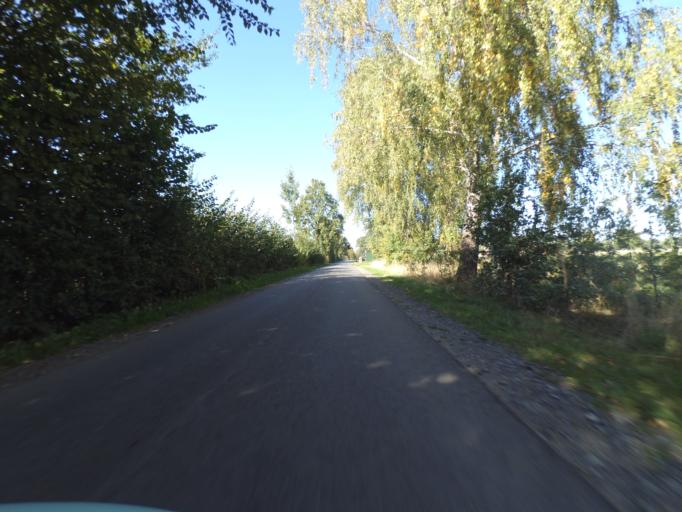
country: DE
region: North Rhine-Westphalia
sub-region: Regierungsbezirk Dusseldorf
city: Bocholt
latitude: 51.8228
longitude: 6.5558
